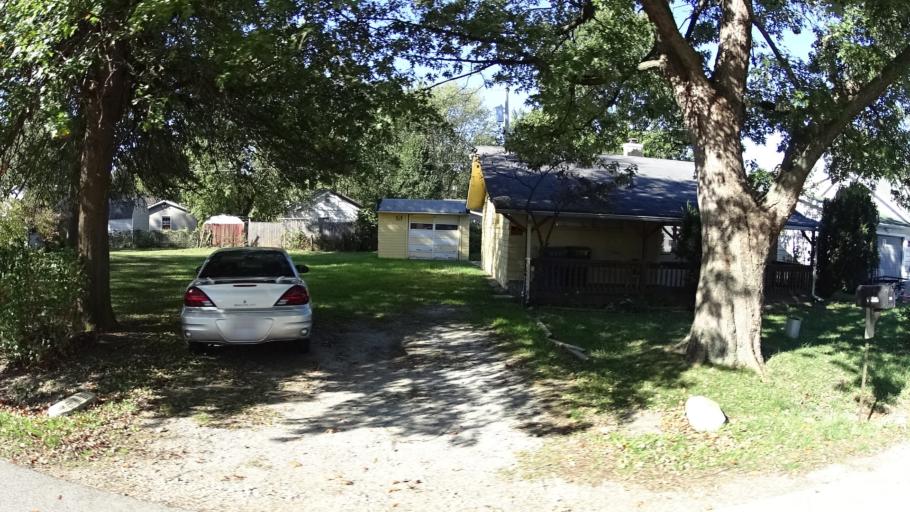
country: US
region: Ohio
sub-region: Lorain County
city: Vermilion-on-the-Lake
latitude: 41.4277
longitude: -82.3224
